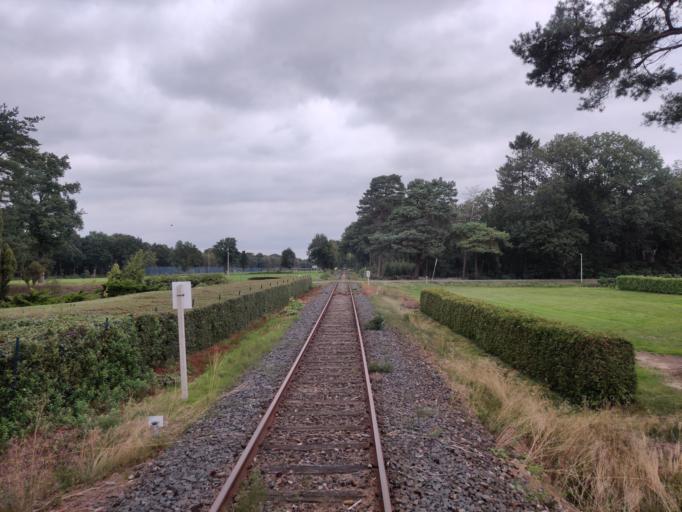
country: DE
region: Lower Saxony
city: Worpswede
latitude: 53.2465
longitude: 8.9592
